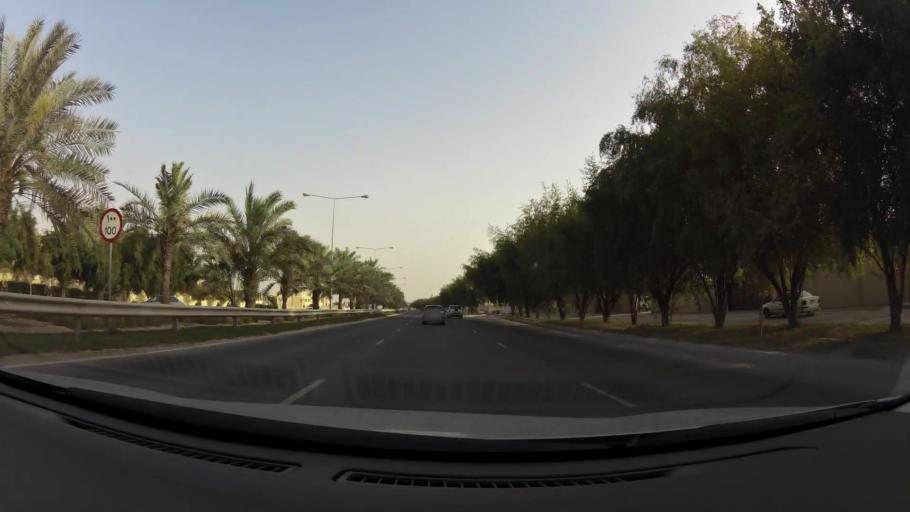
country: QA
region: Baladiyat ar Rayyan
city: Ar Rayyan
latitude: 25.2517
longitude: 51.4584
